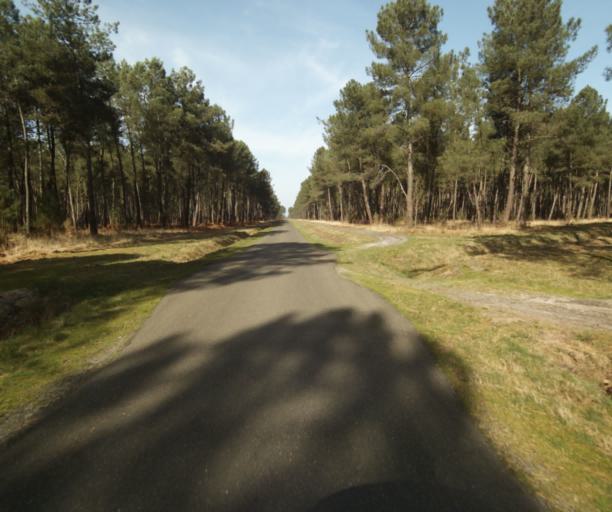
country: FR
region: Aquitaine
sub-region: Departement des Landes
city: Roquefort
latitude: 44.1884
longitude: -0.1914
